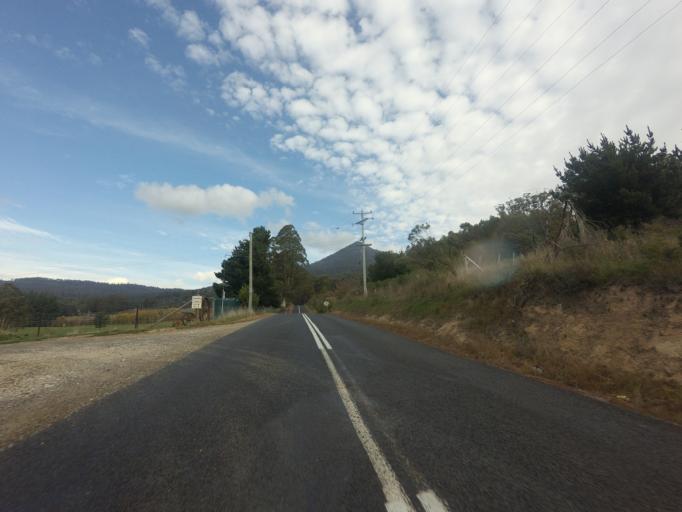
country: AU
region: Tasmania
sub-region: Meander Valley
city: Deloraine
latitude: -41.6253
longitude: 146.7044
